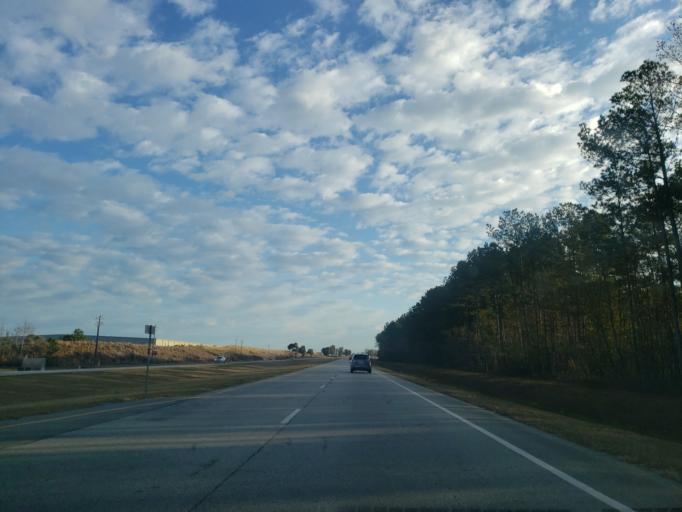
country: US
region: Georgia
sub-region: Chatham County
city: Bloomingdale
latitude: 32.1560
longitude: -81.2745
